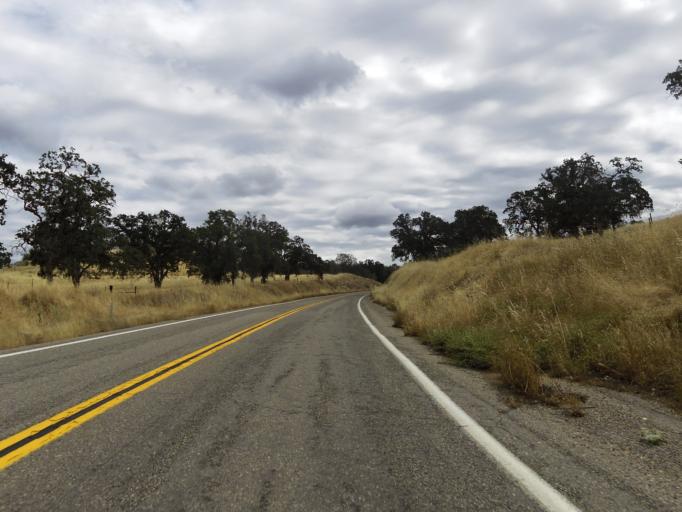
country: US
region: California
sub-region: Madera County
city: Yosemite Lakes
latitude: 37.2308
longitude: -119.8969
